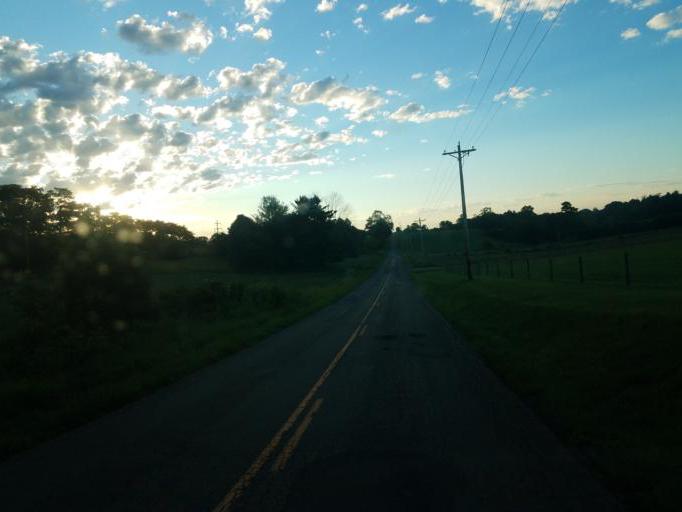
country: US
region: Ohio
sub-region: Sandusky County
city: Bellville
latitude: 40.5391
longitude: -82.4423
